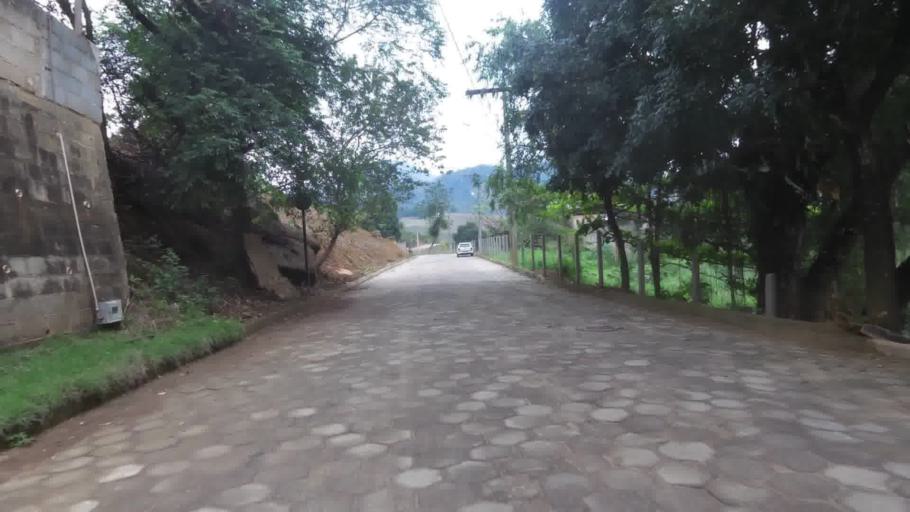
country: BR
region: Espirito Santo
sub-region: Iconha
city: Iconha
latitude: -20.7893
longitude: -40.8189
